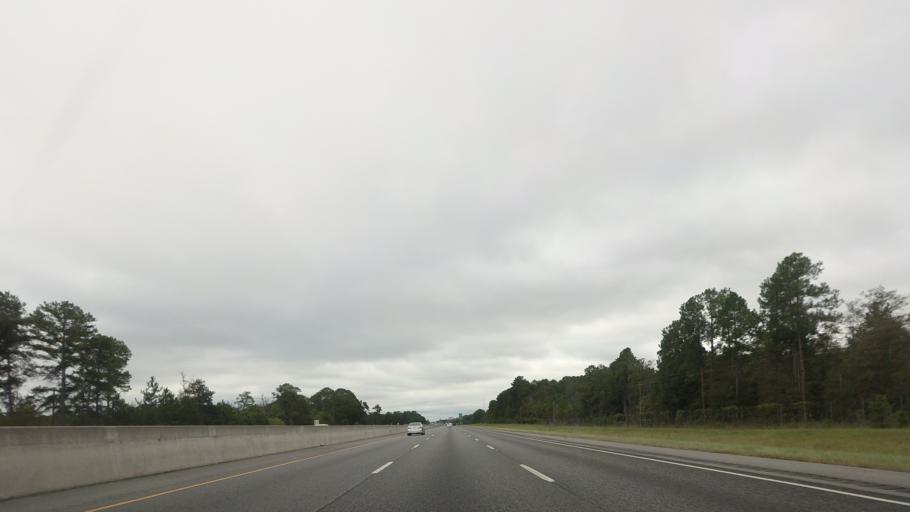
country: US
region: Georgia
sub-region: Lowndes County
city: Hahira
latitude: 31.0128
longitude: -83.3939
